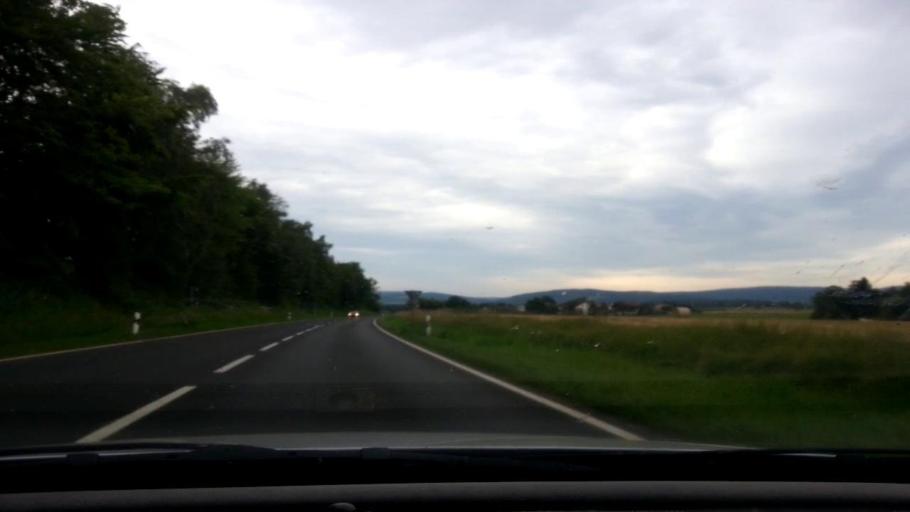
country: DE
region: Bavaria
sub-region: Upper Palatinate
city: Kemnath
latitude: 49.8864
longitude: 11.8835
